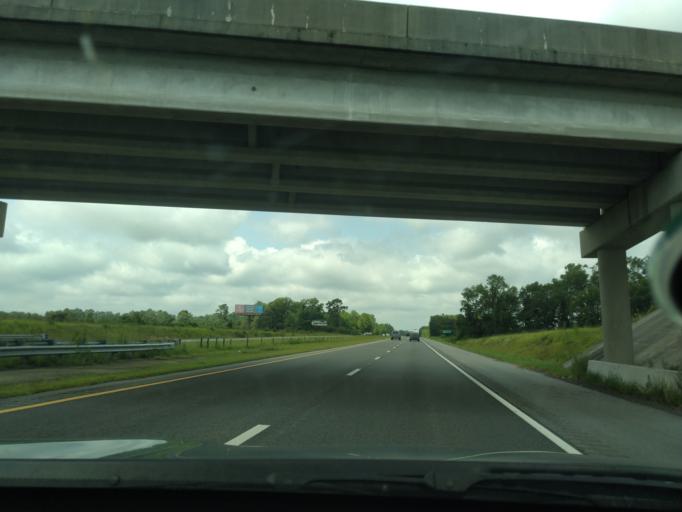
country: US
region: North Carolina
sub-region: Martin County
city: Robersonville
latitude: 35.8338
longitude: -77.2672
